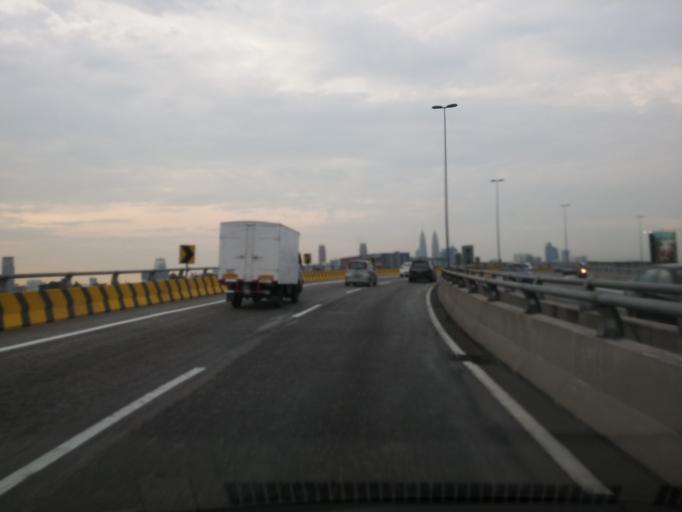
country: MY
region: Kuala Lumpur
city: Kuala Lumpur
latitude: 3.1215
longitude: 101.7161
